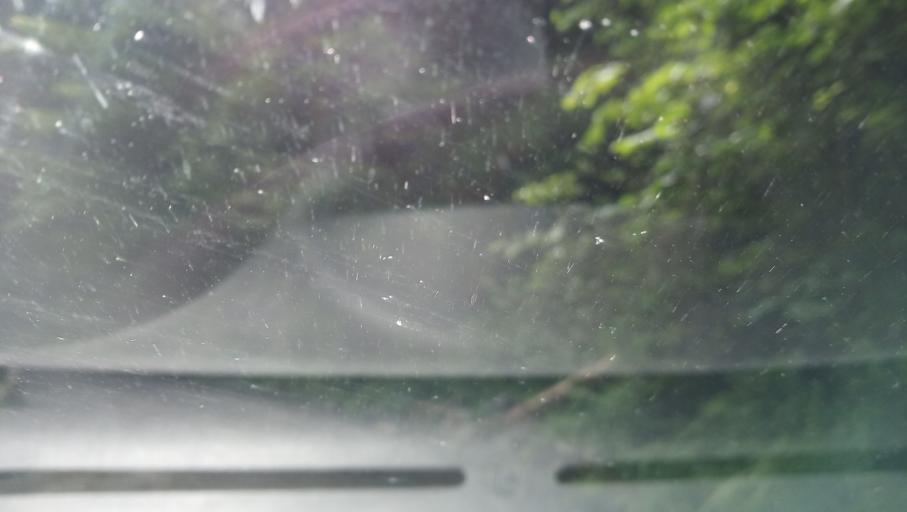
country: RO
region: Hunedoara
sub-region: Oras Petrila
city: Petrila
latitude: 45.4093
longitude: 23.4992
